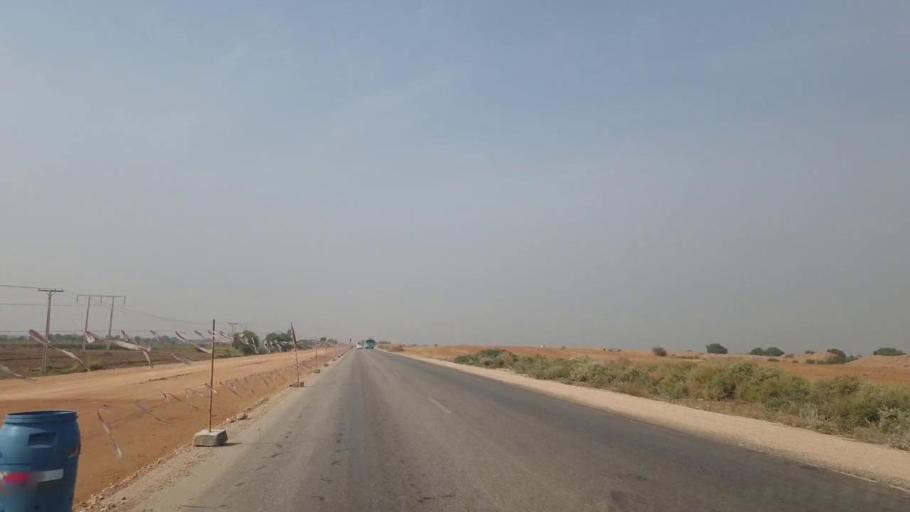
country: PK
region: Sindh
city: Sann
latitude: 26.1272
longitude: 68.0528
